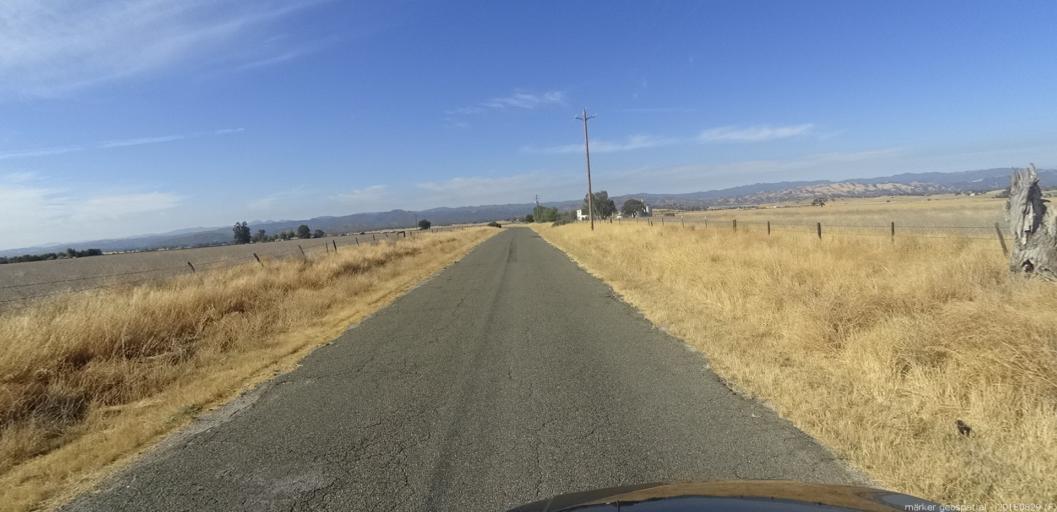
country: US
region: California
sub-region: Monterey County
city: King City
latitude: 35.9734
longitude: -121.0850
